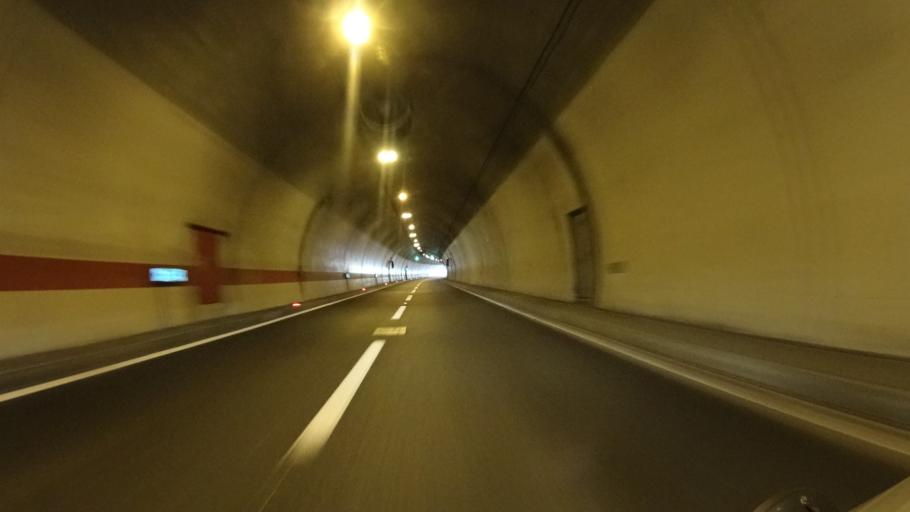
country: HR
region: Primorsko-Goranska
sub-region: Grad Delnice
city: Delnice
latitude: 45.3847
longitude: 14.8034
